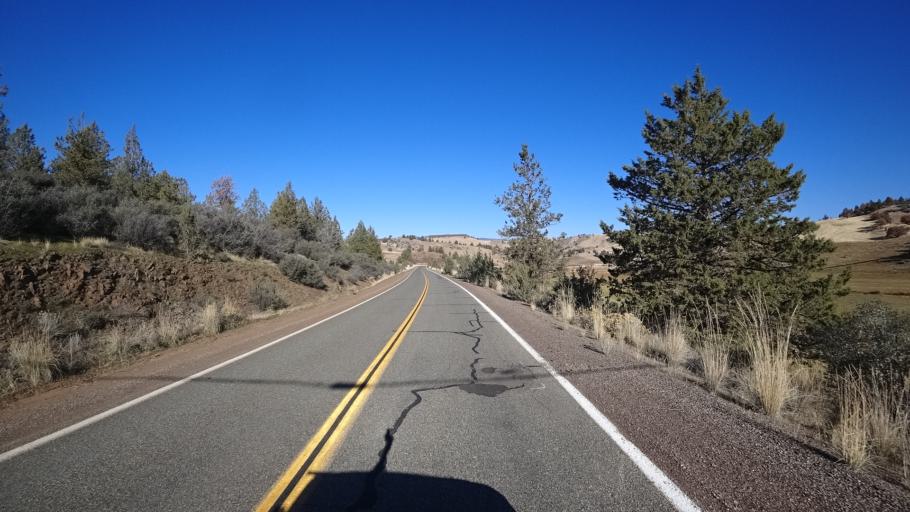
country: US
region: California
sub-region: Siskiyou County
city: Montague
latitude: 41.9141
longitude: -122.3723
